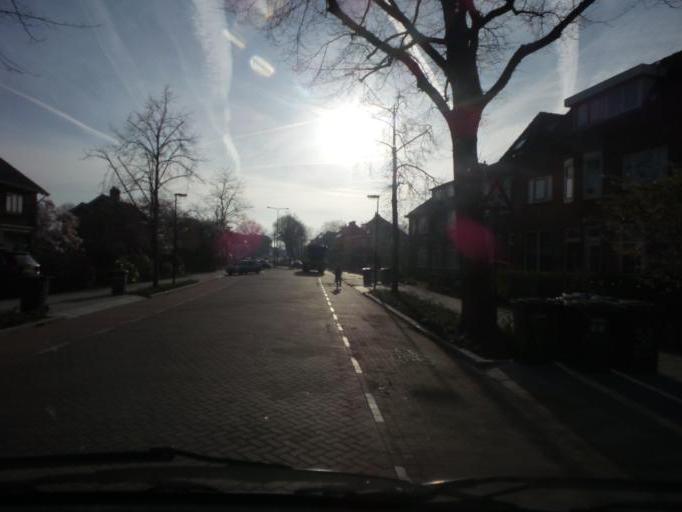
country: NL
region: South Holland
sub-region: Gemeente Gouda
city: Gouda
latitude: 52.0184
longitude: 4.7181
